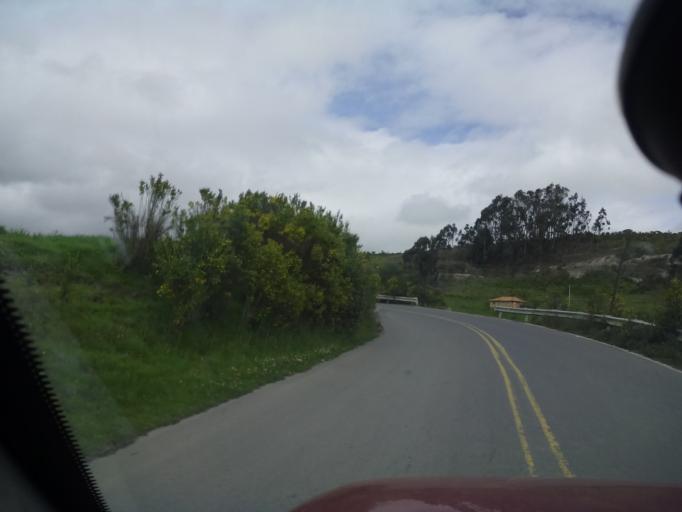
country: CO
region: Boyaca
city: Combita
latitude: 5.6367
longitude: -73.3402
